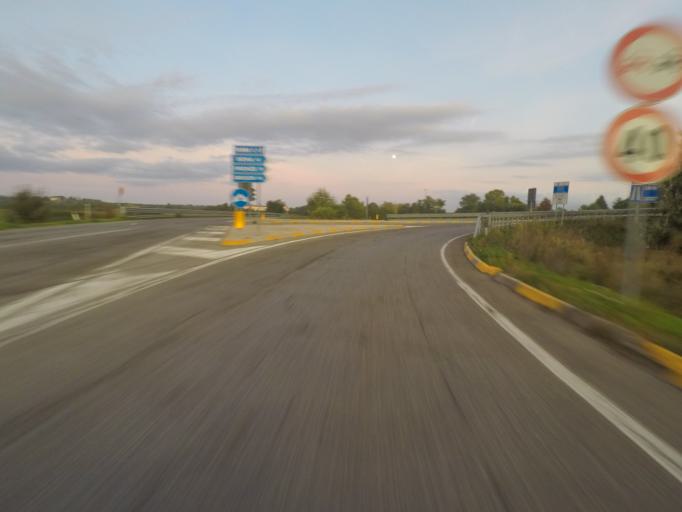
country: IT
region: Tuscany
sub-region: Provincia di Siena
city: Sinalunga
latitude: 43.2237
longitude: 11.7545
